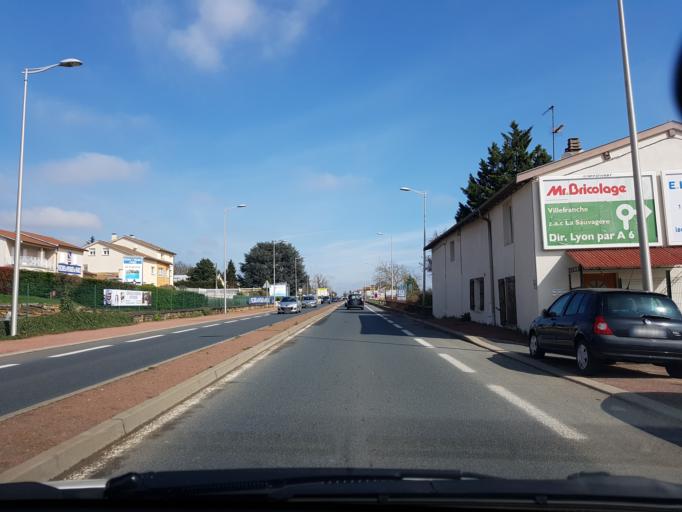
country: FR
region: Rhone-Alpes
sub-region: Departement du Rhone
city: Villefranche-sur-Saone
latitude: 45.9658
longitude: 4.7163
